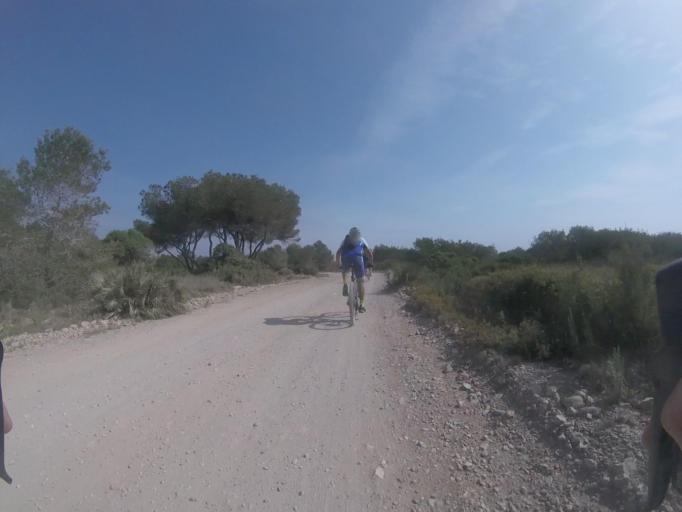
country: ES
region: Valencia
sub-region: Provincia de Castello
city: Santa Magdalena de Pulpis
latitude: 40.2983
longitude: 0.3473
